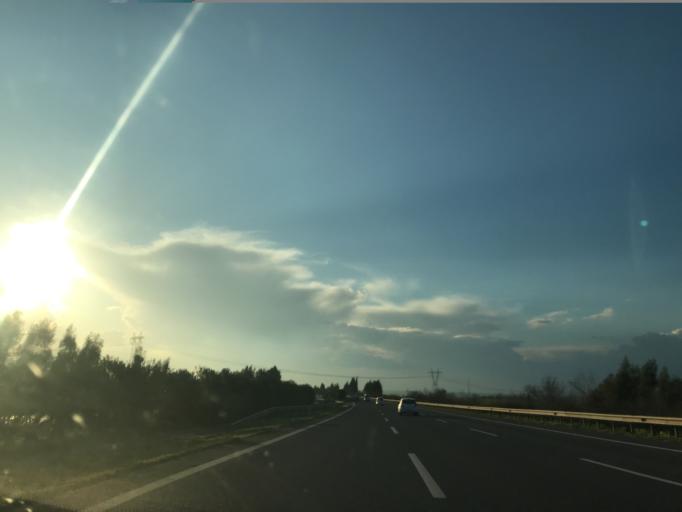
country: TR
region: Adana
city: Ceyhan
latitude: 37.0037
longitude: 35.7208
